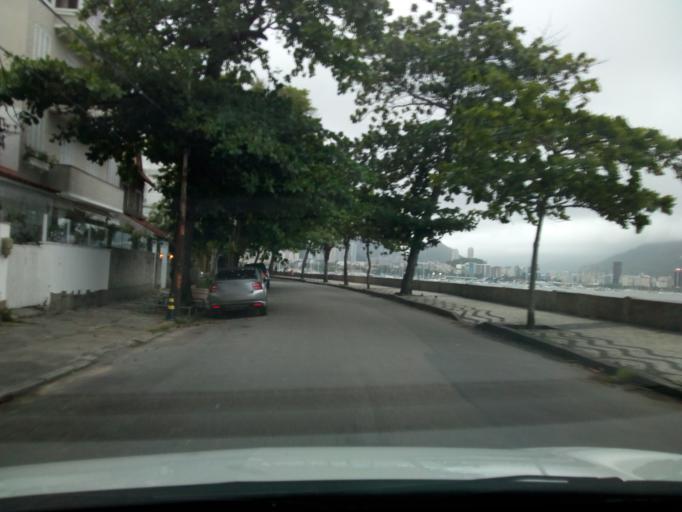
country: BR
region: Rio de Janeiro
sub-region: Rio De Janeiro
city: Rio de Janeiro
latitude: -22.9437
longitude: -43.1620
